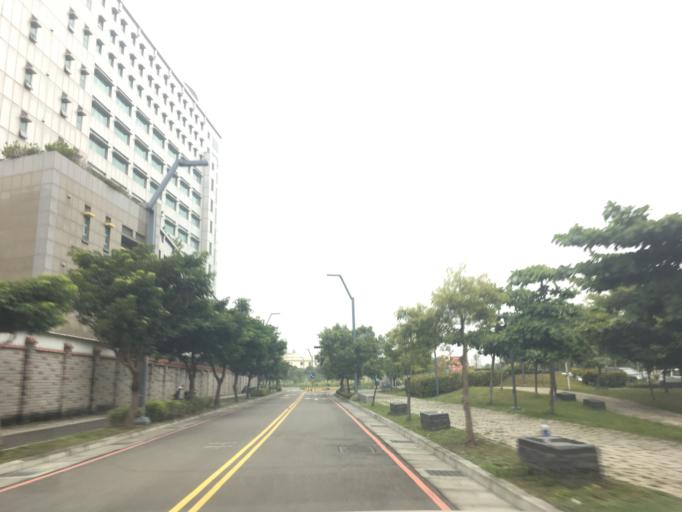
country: TW
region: Taiwan
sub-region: Taichung City
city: Taichung
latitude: 24.1907
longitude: 120.6453
